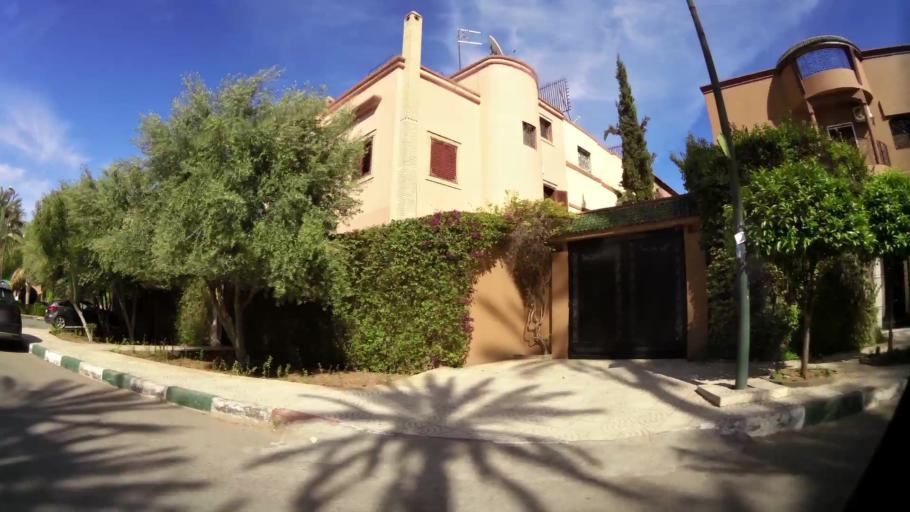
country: MA
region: Marrakech-Tensift-Al Haouz
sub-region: Marrakech
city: Marrakesh
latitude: 31.6534
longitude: -8.0145
